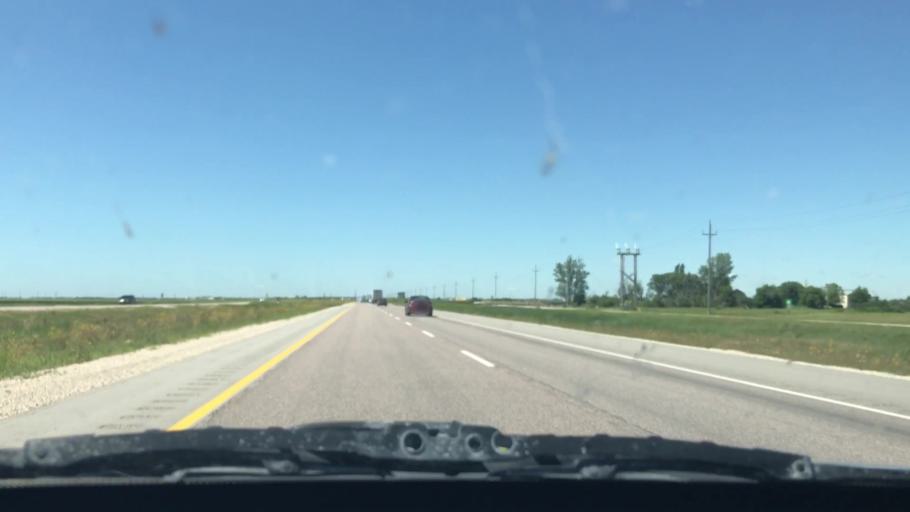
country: CA
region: Manitoba
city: Steinbach
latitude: 49.6889
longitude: -96.6152
